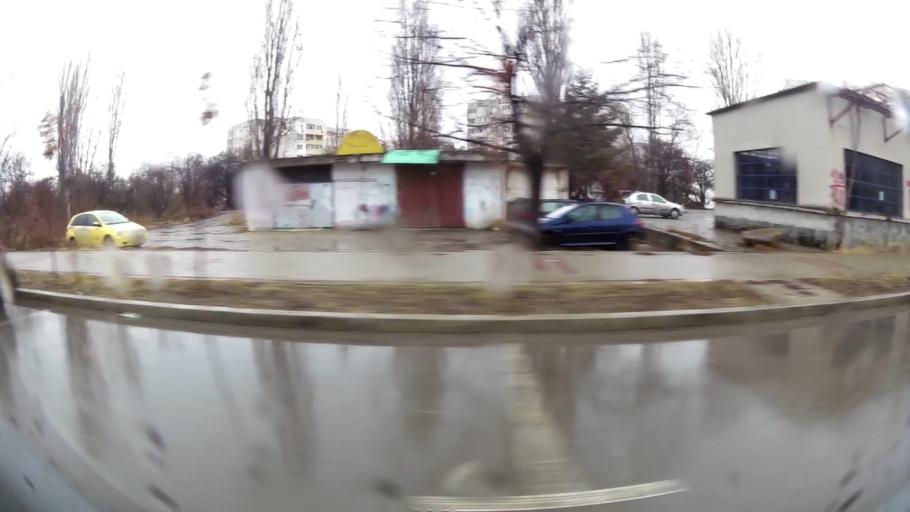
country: BG
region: Sofia-Capital
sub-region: Stolichna Obshtina
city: Sofia
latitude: 42.6496
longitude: 23.3993
